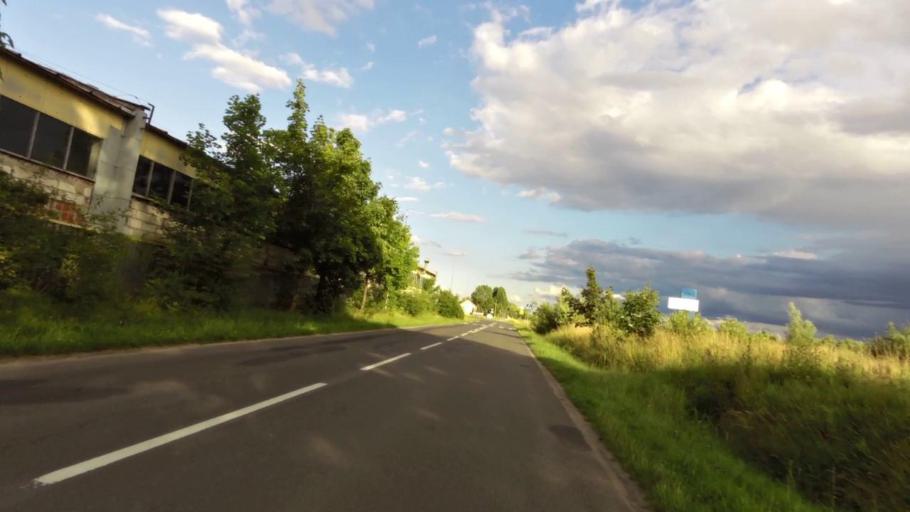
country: PL
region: West Pomeranian Voivodeship
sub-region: Powiat slawienski
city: Darlowo
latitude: 54.4140
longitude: 16.4039
